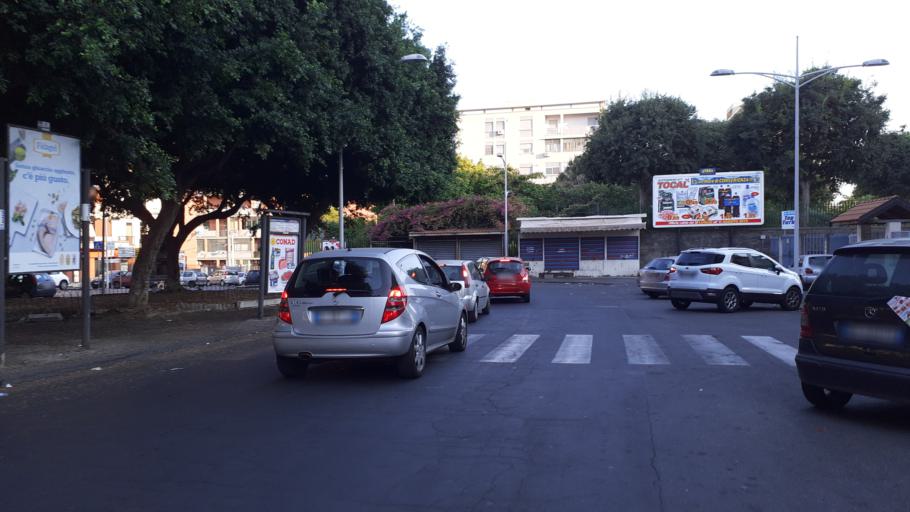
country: IT
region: Sicily
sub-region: Catania
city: Catania
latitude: 37.5012
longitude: 15.0698
